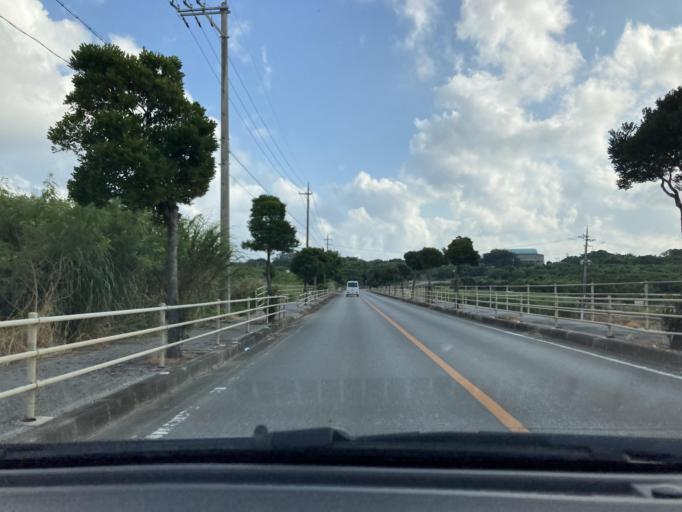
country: JP
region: Okinawa
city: Itoman
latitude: 26.0982
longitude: 127.6656
